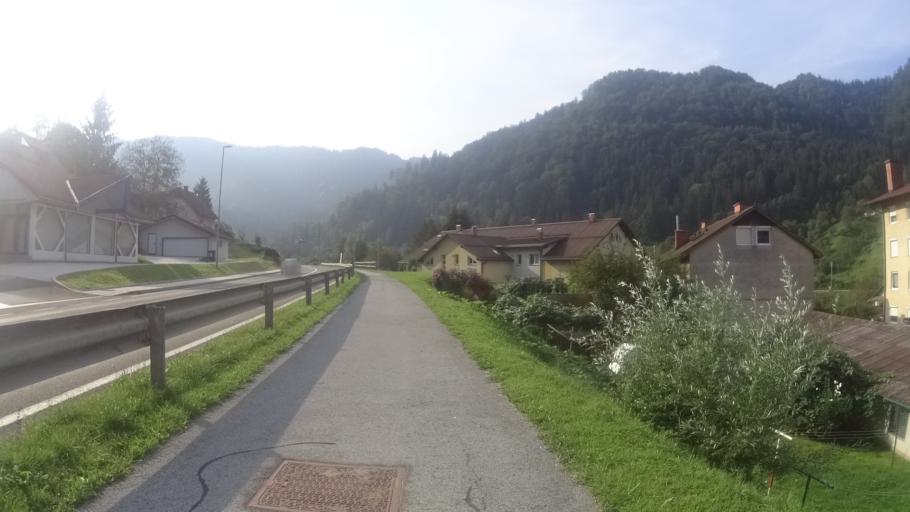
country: SI
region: Podvelka
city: Podvelka
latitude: 46.5920
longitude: 15.3195
